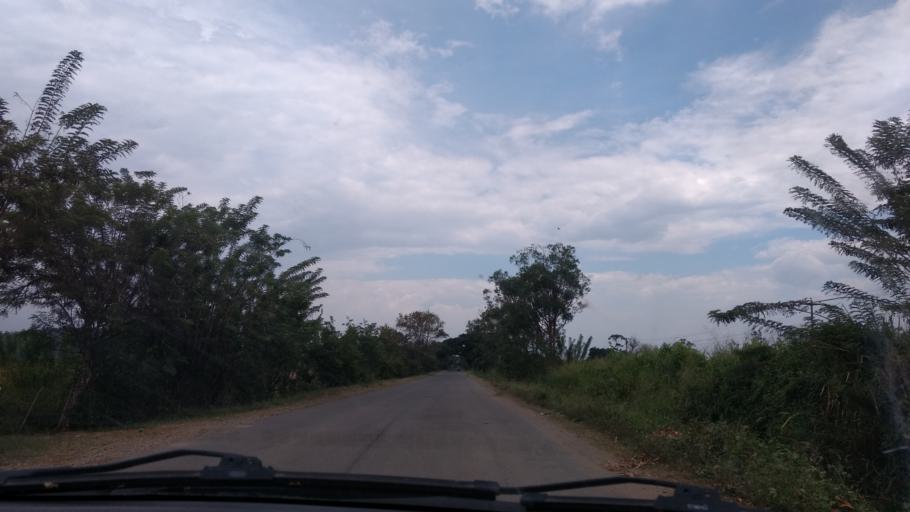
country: CO
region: Cauca
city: Buenos Aires
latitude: 3.1185
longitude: -76.6205
